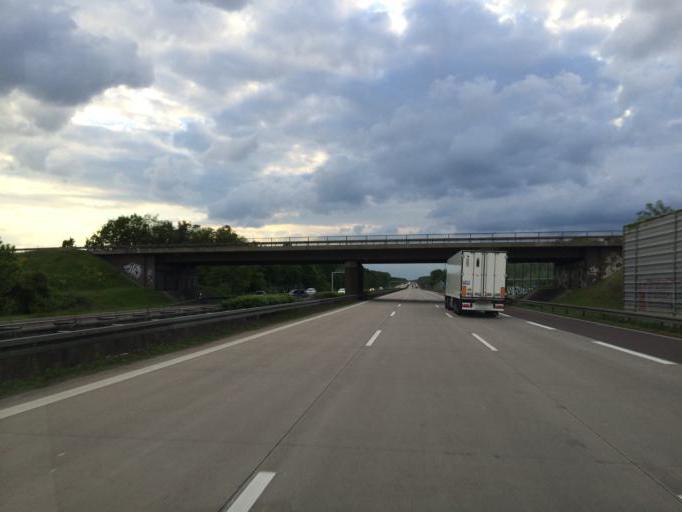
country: DE
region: Saxony-Anhalt
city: Schermen
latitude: 52.2258
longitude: 11.8232
